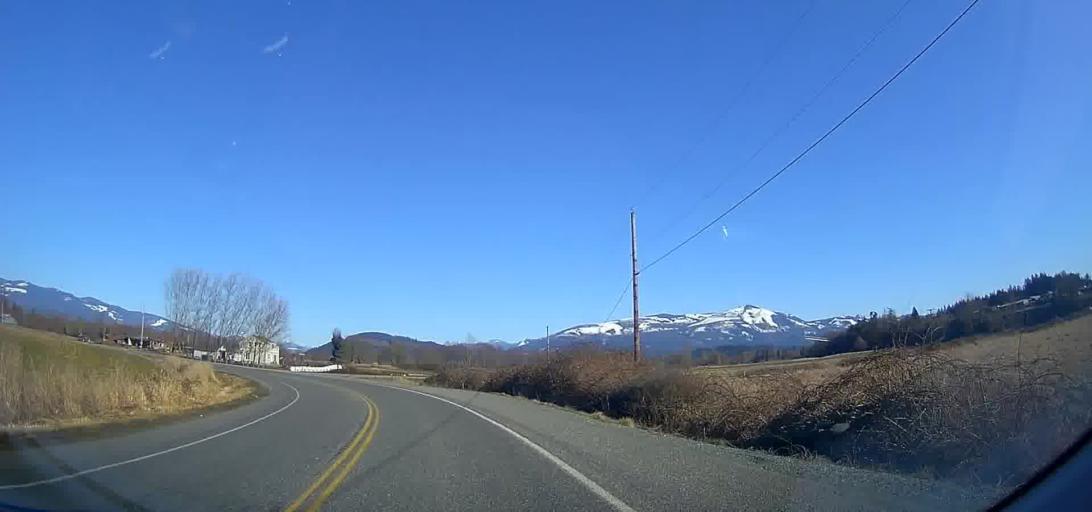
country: US
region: Washington
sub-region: Skagit County
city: Burlington
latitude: 48.4651
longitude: -122.3000
